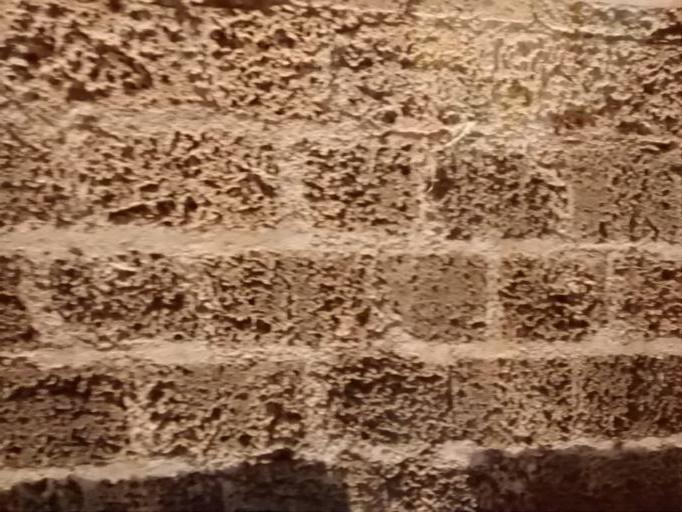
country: CO
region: Bolivar
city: Cartagena
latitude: 10.4208
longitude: -75.5440
